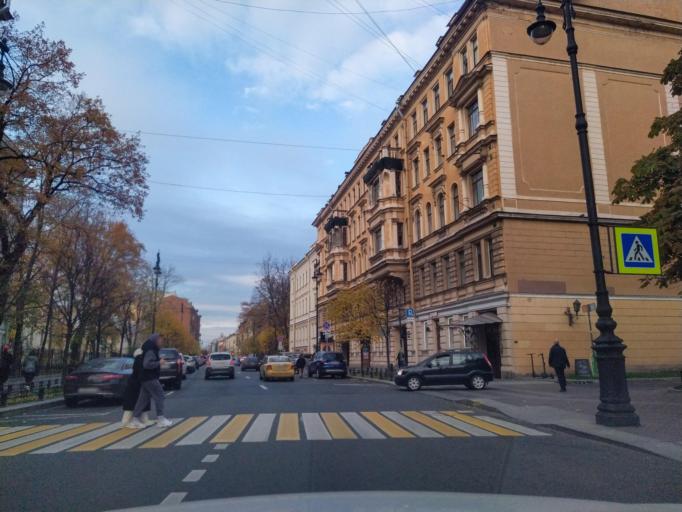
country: RU
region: St.-Petersburg
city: Centralniy
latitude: 59.9335
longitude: 30.3545
